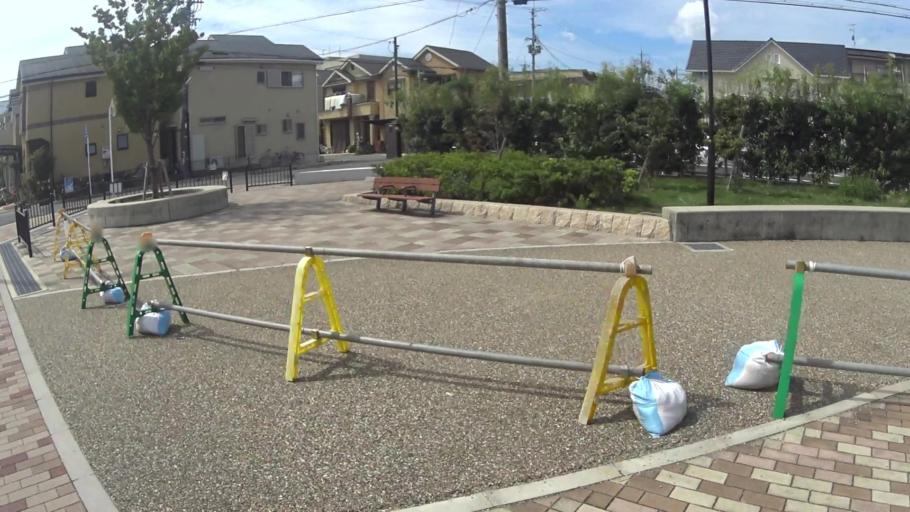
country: JP
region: Kyoto
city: Muko
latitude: 34.9599
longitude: 135.7063
